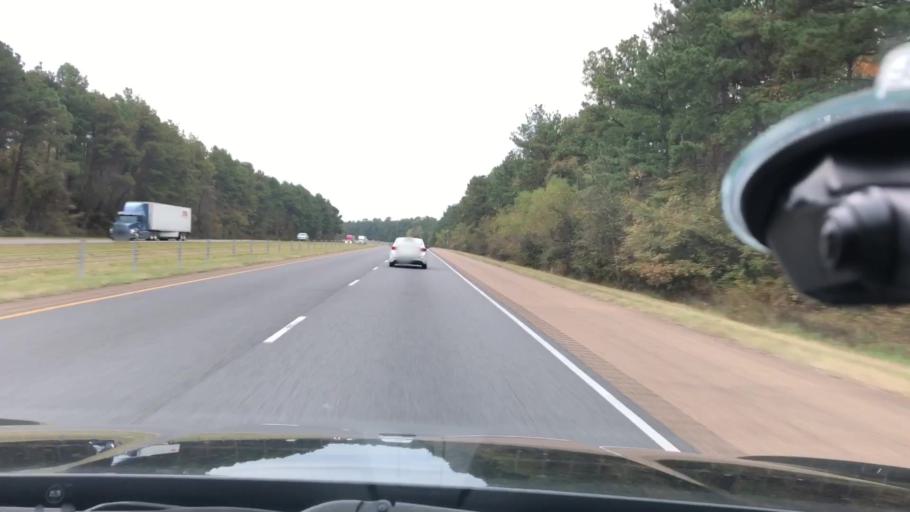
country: US
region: Arkansas
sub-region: Clark County
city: Gurdon
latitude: 33.9541
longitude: -93.2289
